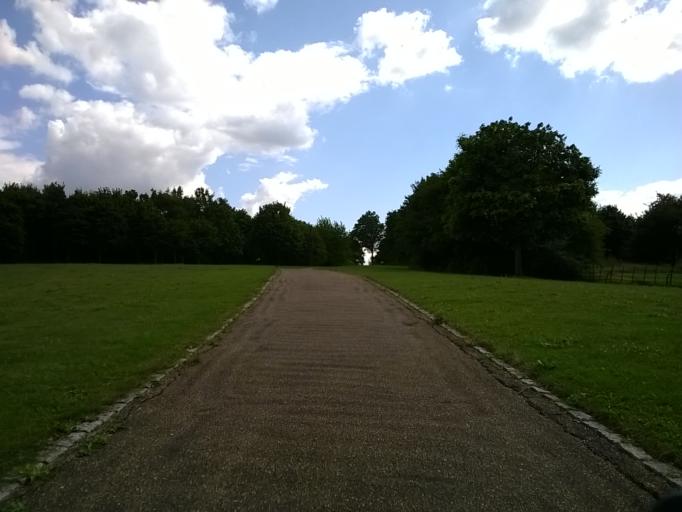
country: GB
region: England
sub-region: Milton Keynes
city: Milton Keynes
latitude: 52.0489
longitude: -0.7390
